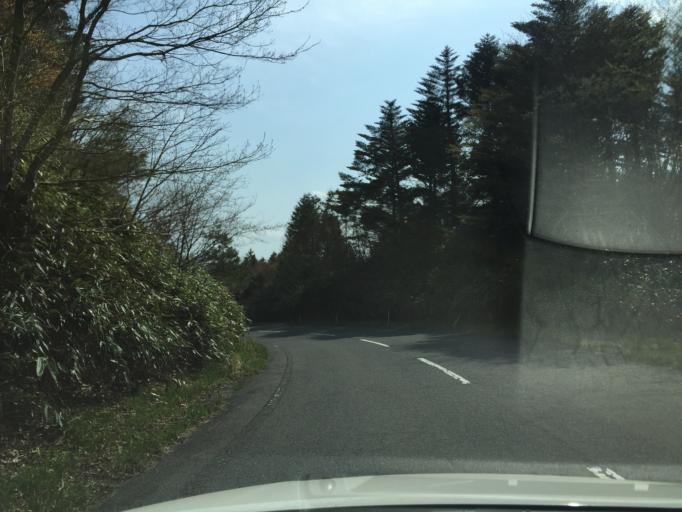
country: JP
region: Fukushima
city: Iwaki
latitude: 37.2109
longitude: 140.8578
